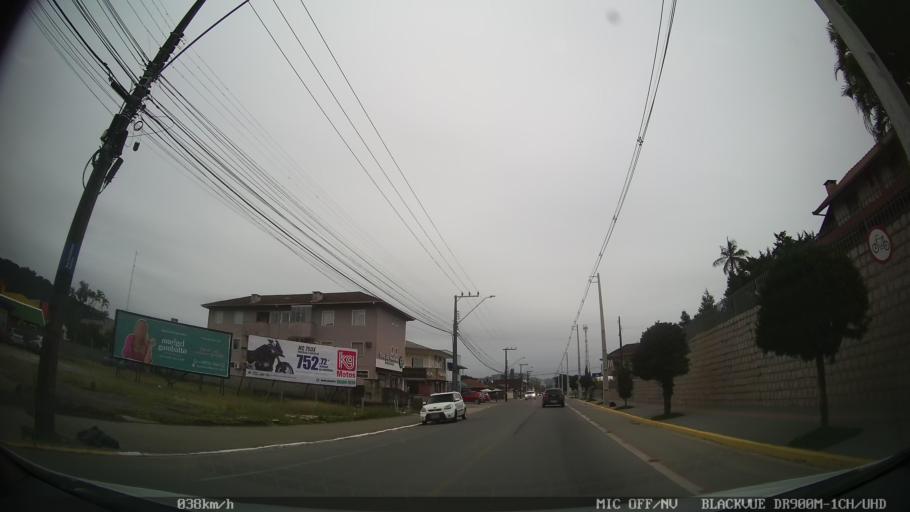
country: BR
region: Santa Catarina
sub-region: Joinville
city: Joinville
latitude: -26.2096
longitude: -48.9072
